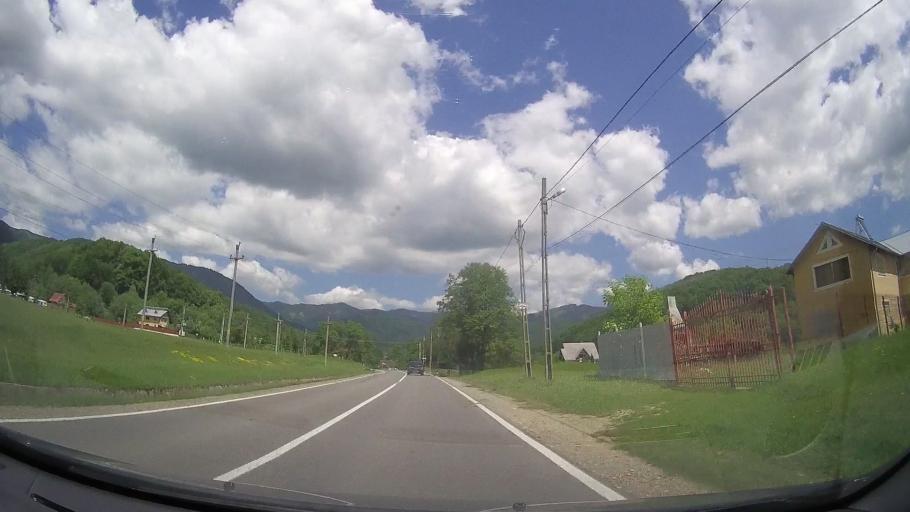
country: RO
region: Prahova
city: Maneciu
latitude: 45.4416
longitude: 25.9388
